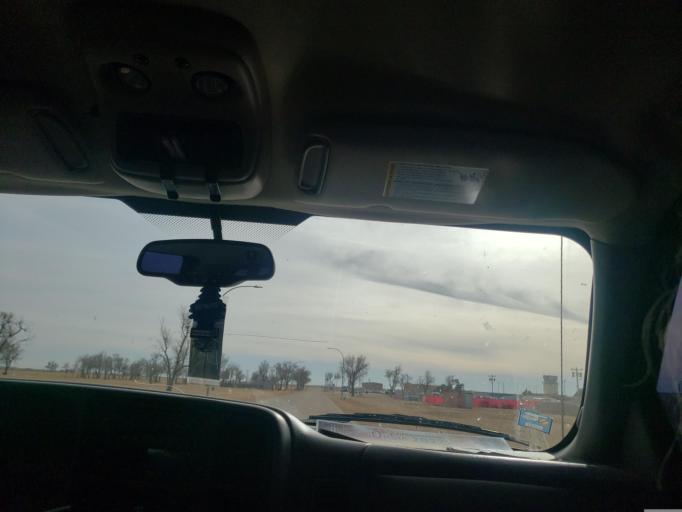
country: US
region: Kansas
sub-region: Finney County
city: Garden City
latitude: 37.9299
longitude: -100.7183
